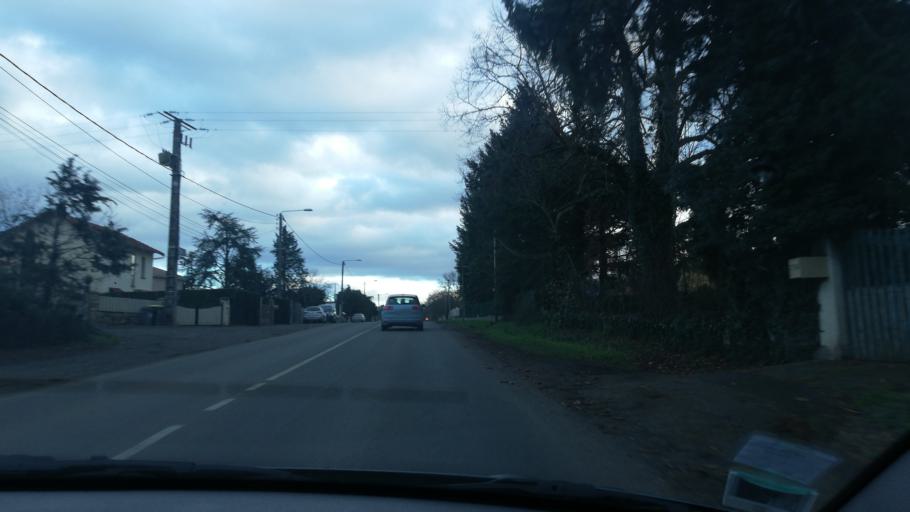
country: FR
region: Auvergne
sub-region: Departement du Puy-de-Dome
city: Vertaizon
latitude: 45.7812
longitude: 3.2889
